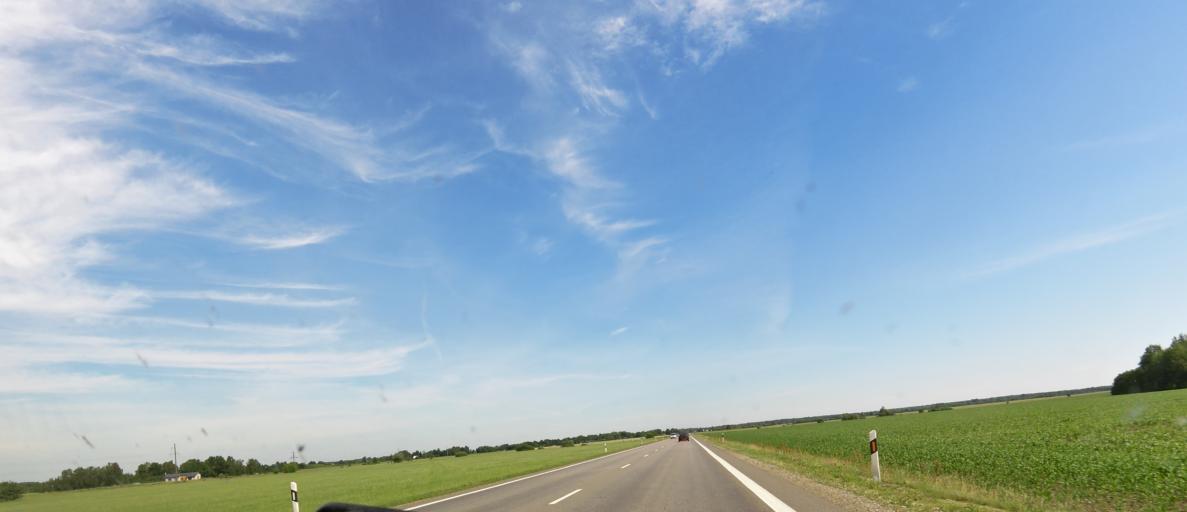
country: LT
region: Panevezys
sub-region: Panevezys City
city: Panevezys
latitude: 55.7838
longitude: 24.3088
